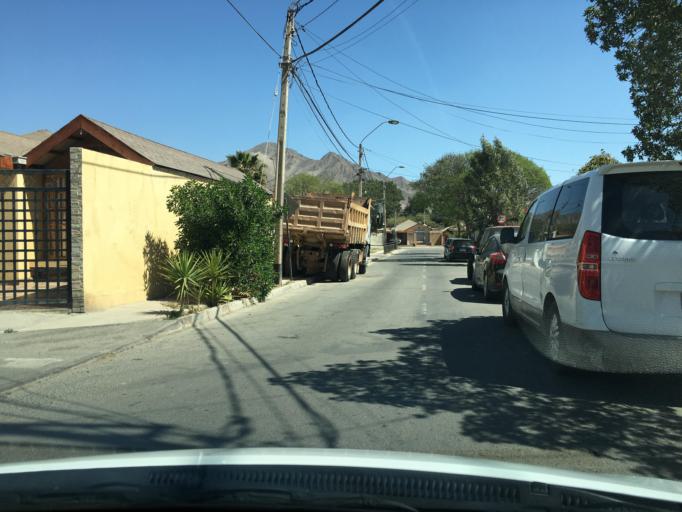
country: CL
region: Atacama
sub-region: Provincia de Copiapo
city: Copiapo
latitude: -27.4111
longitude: -70.2860
